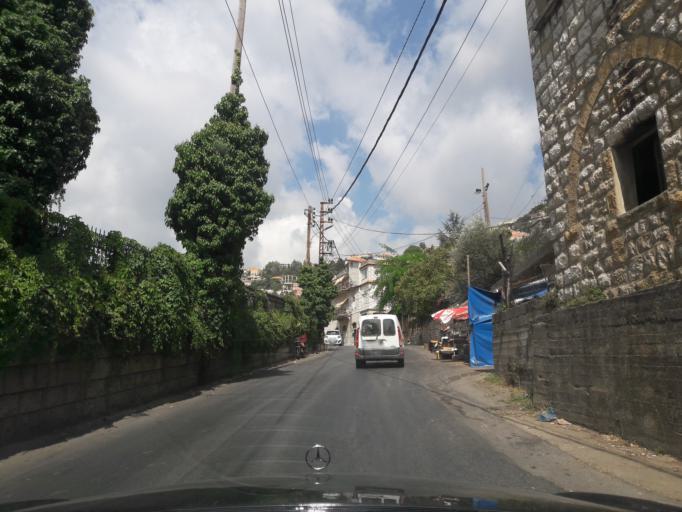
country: LB
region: Mont-Liban
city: Djounie
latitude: 33.9283
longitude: 35.6703
